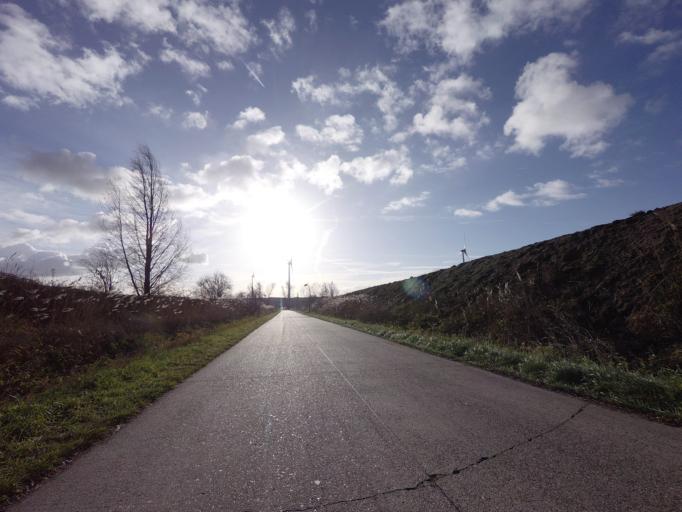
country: BE
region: Flanders
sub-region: Provincie Antwerpen
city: Stabroek
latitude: 51.2991
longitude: 4.3539
